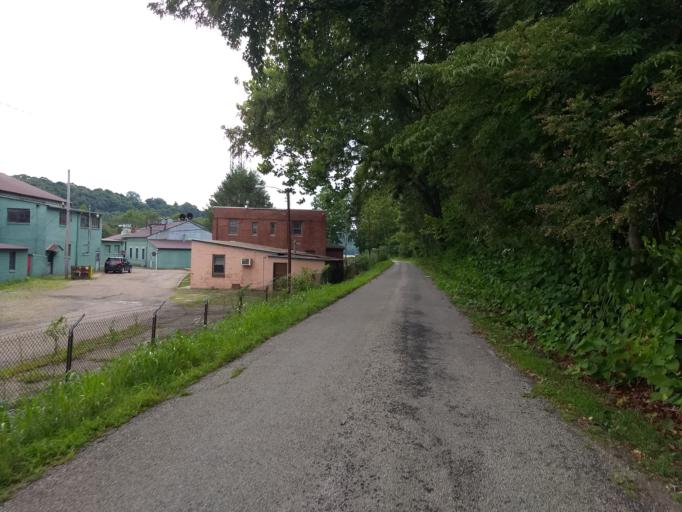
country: US
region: Pennsylvania
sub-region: Allegheny County
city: Brackenridge
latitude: 40.6141
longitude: -79.7140
